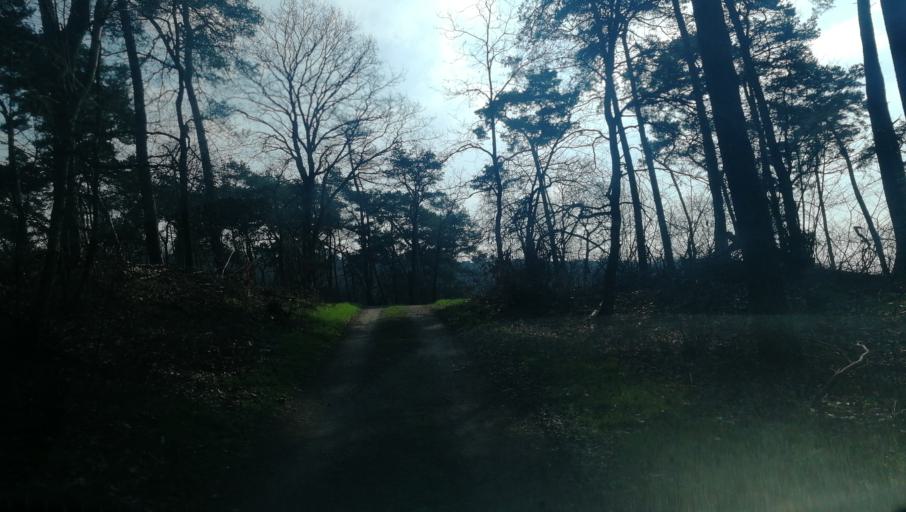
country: NL
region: Limburg
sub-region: Gemeente Venlo
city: Venlo
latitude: 51.3987
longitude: 6.1806
